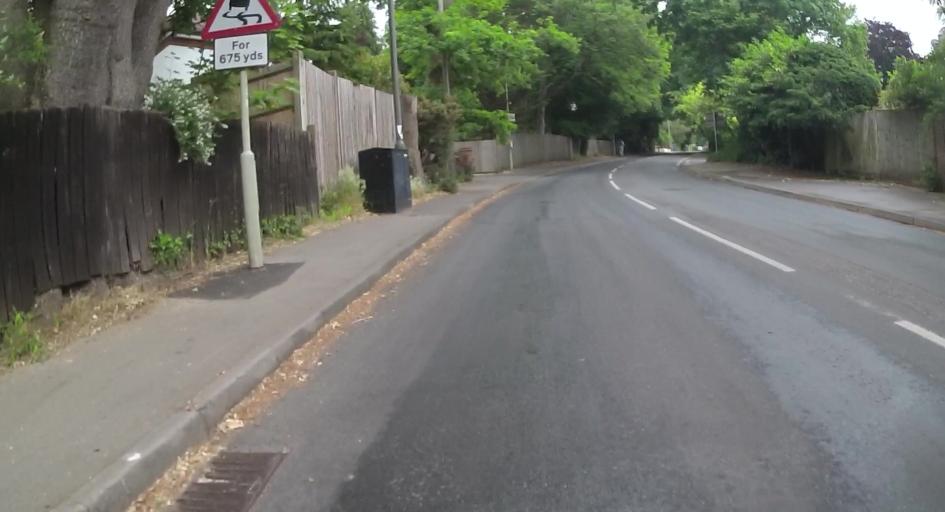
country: GB
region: England
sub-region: Hampshire
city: Fleet
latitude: 51.2627
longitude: -0.8487
